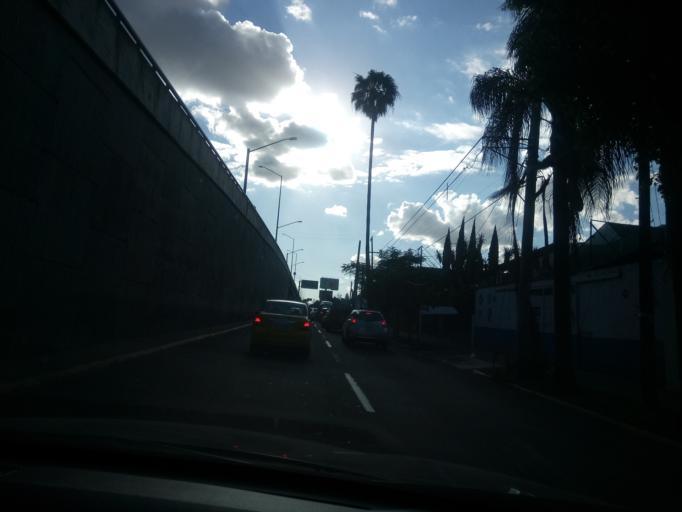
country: MX
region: Jalisco
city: Guadalajara
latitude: 20.6604
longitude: -103.3822
